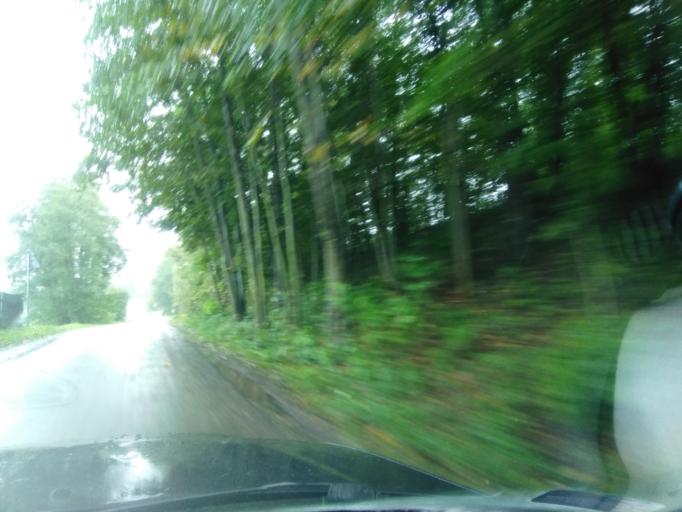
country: PL
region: Subcarpathian Voivodeship
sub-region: Powiat ropczycko-sedziszowski
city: Niedzwiada
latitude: 50.0209
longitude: 21.5411
